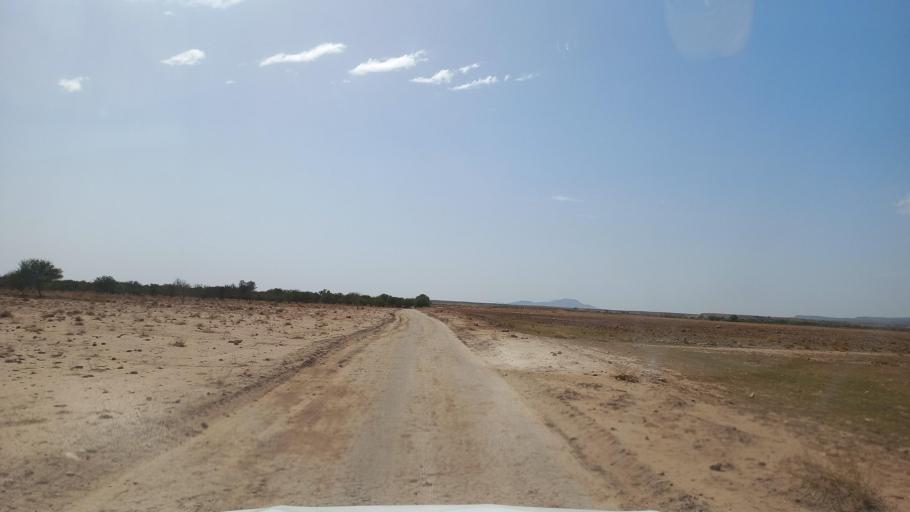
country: TN
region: Al Qasrayn
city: Kasserine
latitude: 35.2570
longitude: 8.9684
